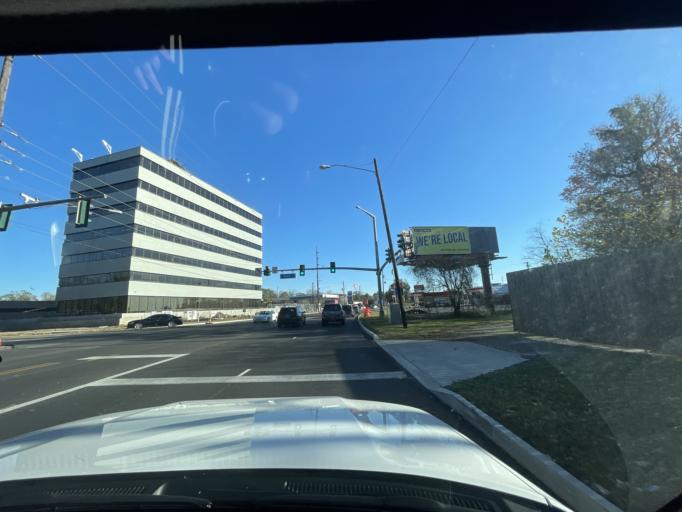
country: US
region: Louisiana
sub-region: East Baton Rouge Parish
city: Baton Rouge
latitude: 30.4271
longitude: -91.1513
